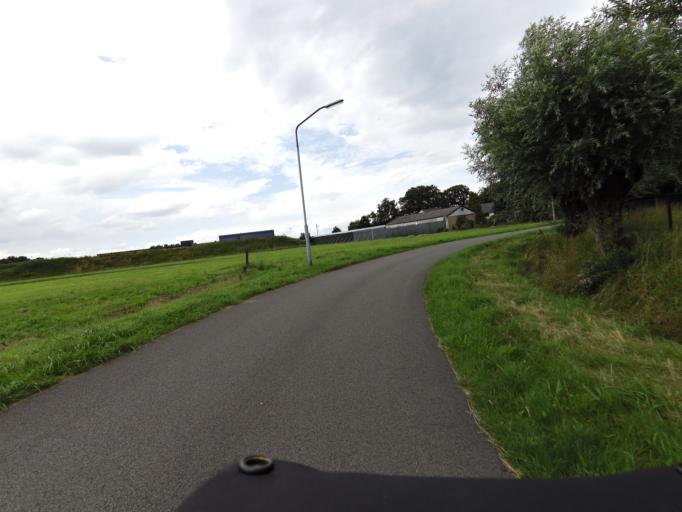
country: NL
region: North Brabant
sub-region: Gemeente Breda
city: Breda
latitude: 51.5880
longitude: 4.7381
